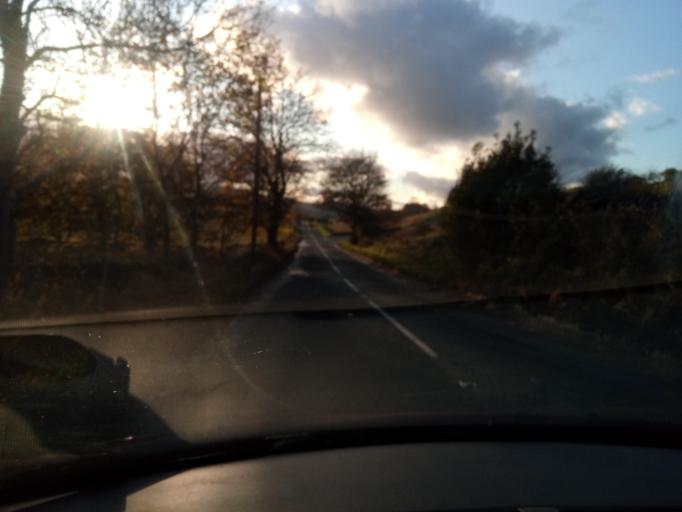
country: GB
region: England
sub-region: County Durham
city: Stanhope
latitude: 54.7399
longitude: -2.1039
